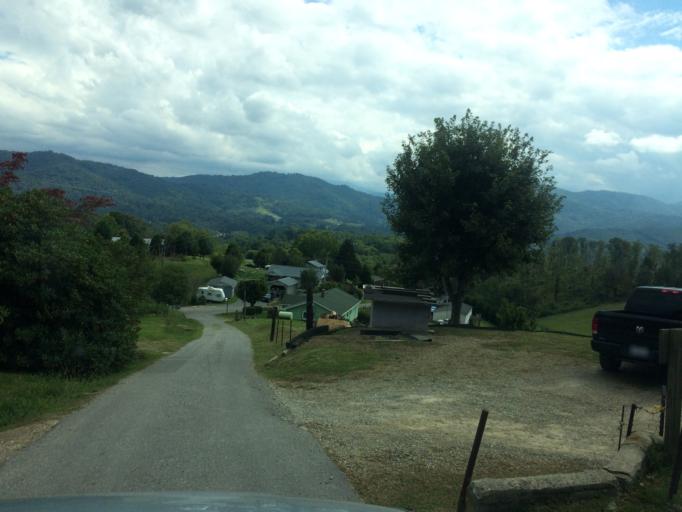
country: US
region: North Carolina
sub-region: Haywood County
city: Clyde
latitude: 35.5512
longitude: -82.9123
